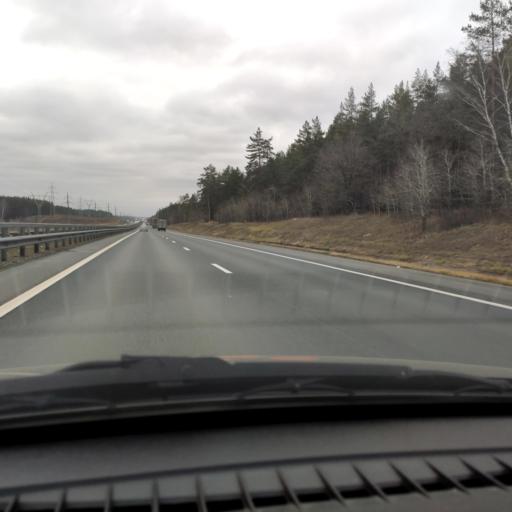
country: RU
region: Samara
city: Povolzhskiy
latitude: 53.5167
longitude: 49.7441
